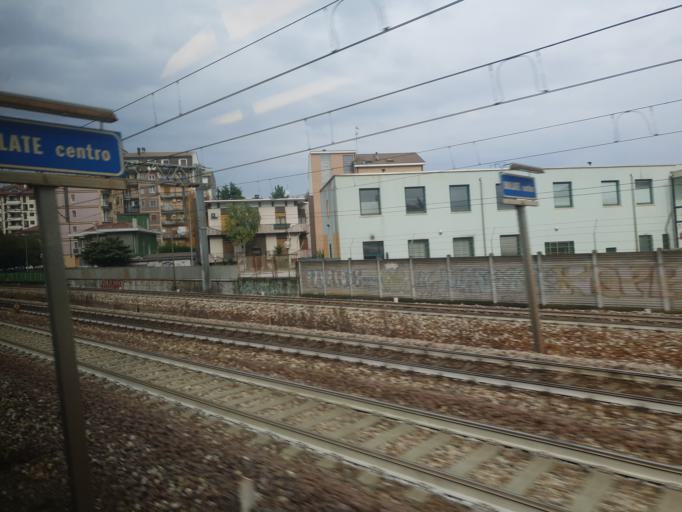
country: IT
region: Lombardy
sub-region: Citta metropolitana di Milano
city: Bollate
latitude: 45.5413
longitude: 9.1244
